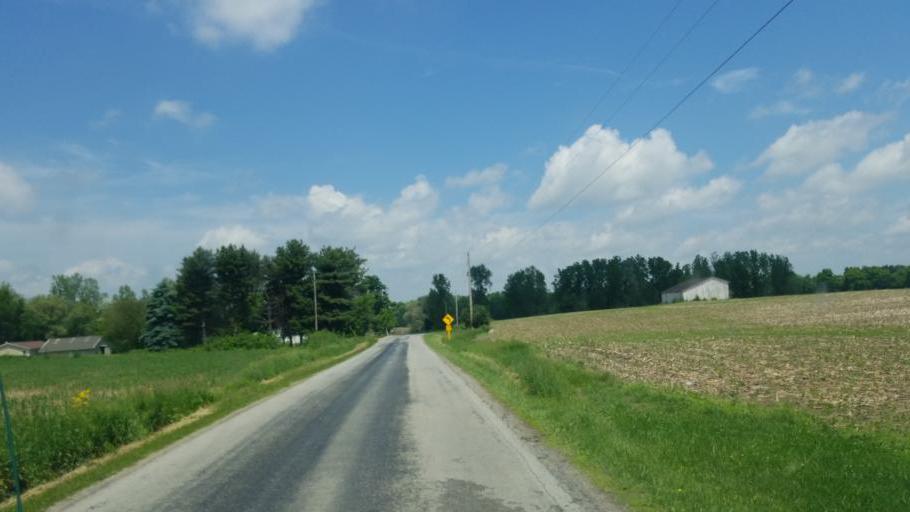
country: US
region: Ohio
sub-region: Ashland County
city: Ashland
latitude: 40.8318
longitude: -82.2507
